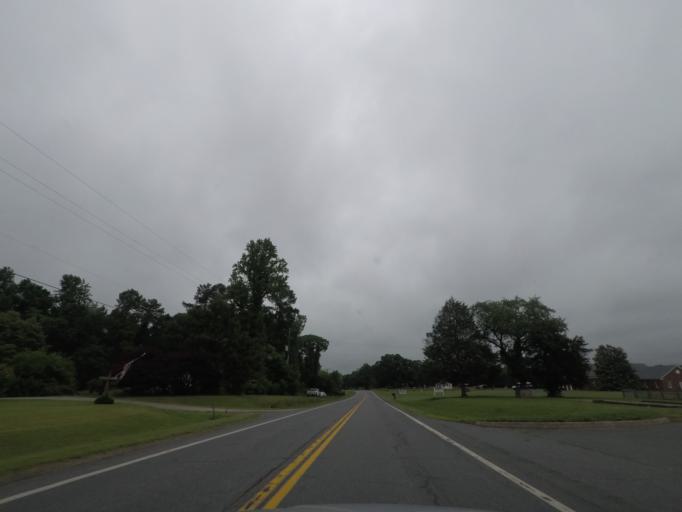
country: US
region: Virginia
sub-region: Fluvanna County
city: Weber City
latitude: 37.6682
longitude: -78.3431
